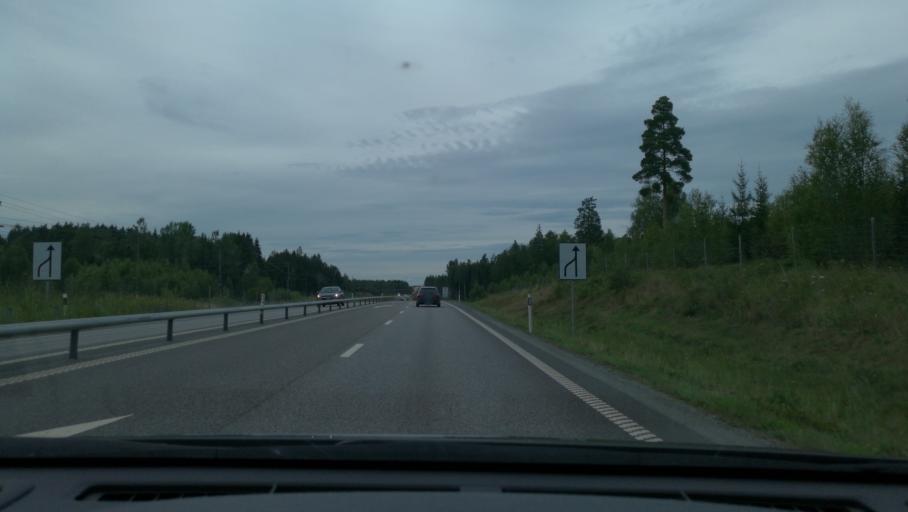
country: SE
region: Soedermanland
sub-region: Katrineholms Kommun
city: Katrineholm
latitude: 58.9154
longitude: 16.1980
